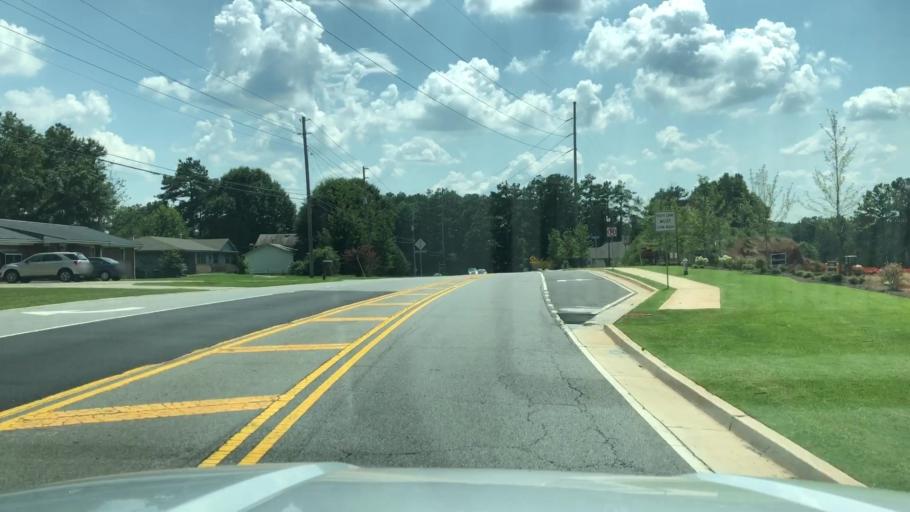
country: US
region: Georgia
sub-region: Cobb County
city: Acworth
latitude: 34.0337
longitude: -84.6928
